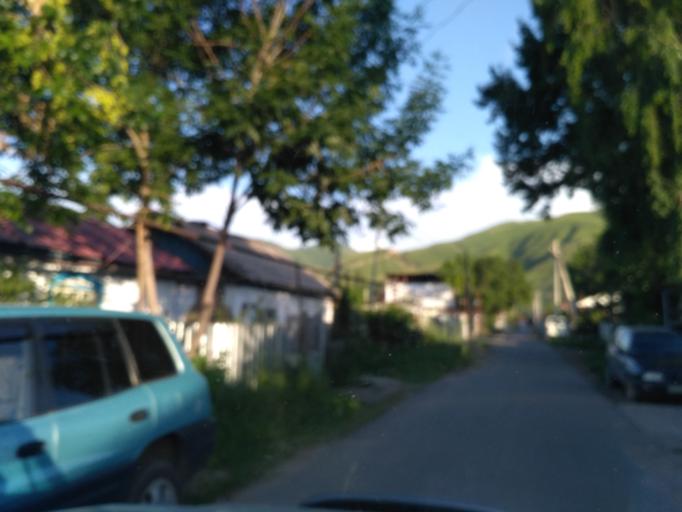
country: KZ
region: Almaty Oblysy
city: Burunday
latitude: 43.1631
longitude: 76.4070
